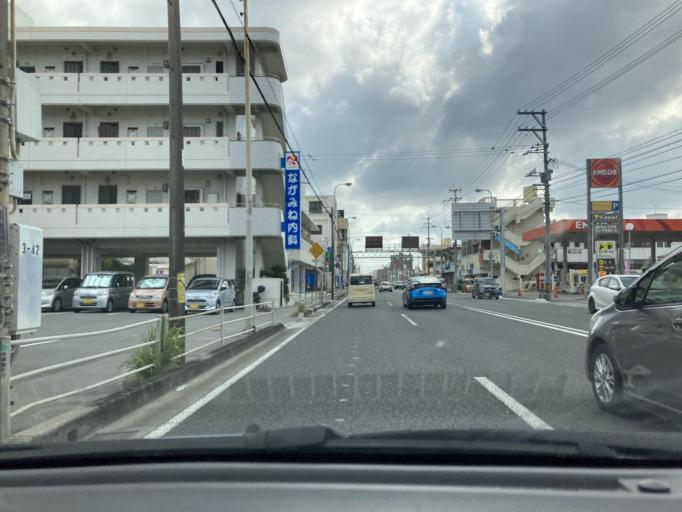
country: JP
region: Okinawa
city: Ginowan
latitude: 26.2110
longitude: 127.7596
